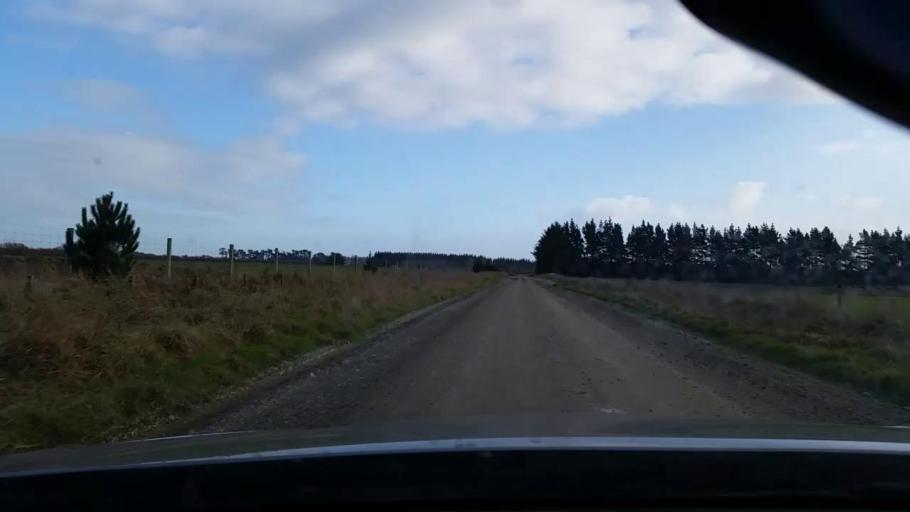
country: NZ
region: Southland
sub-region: Southland District
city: Winton
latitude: -46.2736
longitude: 168.2879
